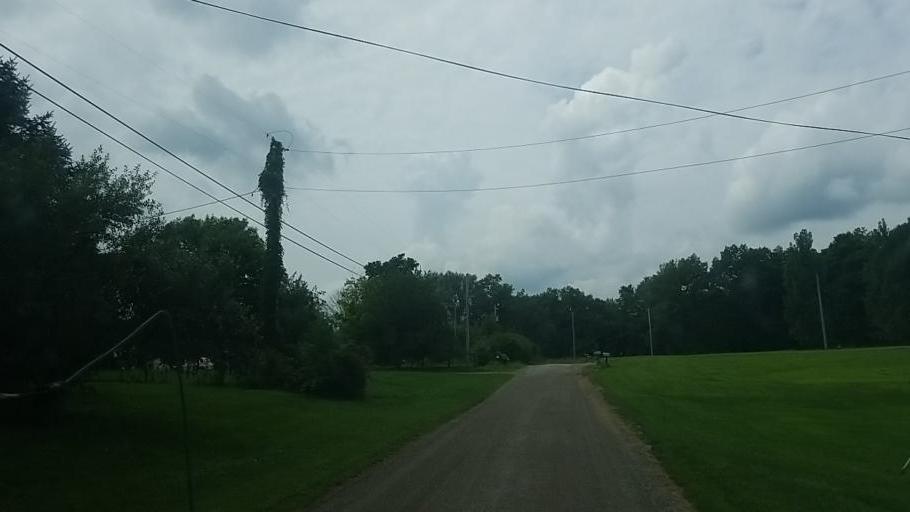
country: US
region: Ohio
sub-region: Licking County
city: Utica
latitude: 40.1932
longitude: -82.3267
